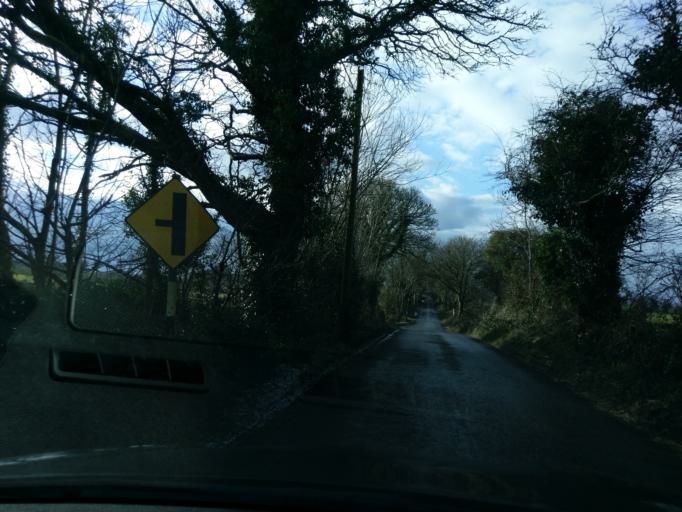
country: IE
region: Connaught
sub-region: County Galway
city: Athenry
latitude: 53.3873
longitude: -8.6021
